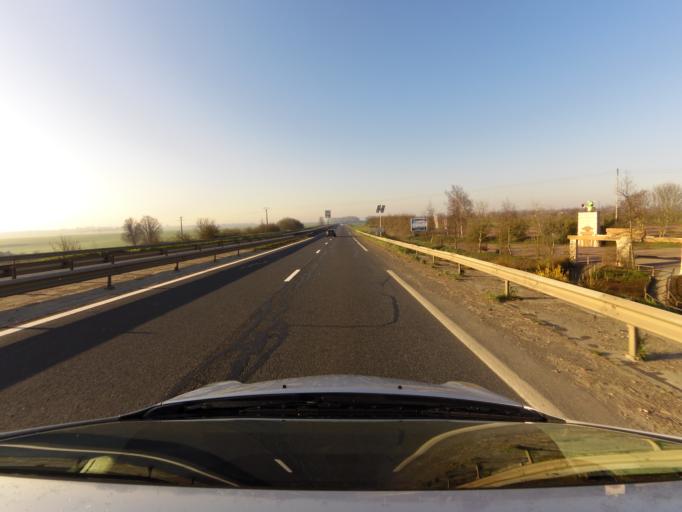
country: FR
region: Lower Normandy
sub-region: Departement du Calvados
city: Bretteville-sur-Odon
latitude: 49.1843
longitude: -0.4255
